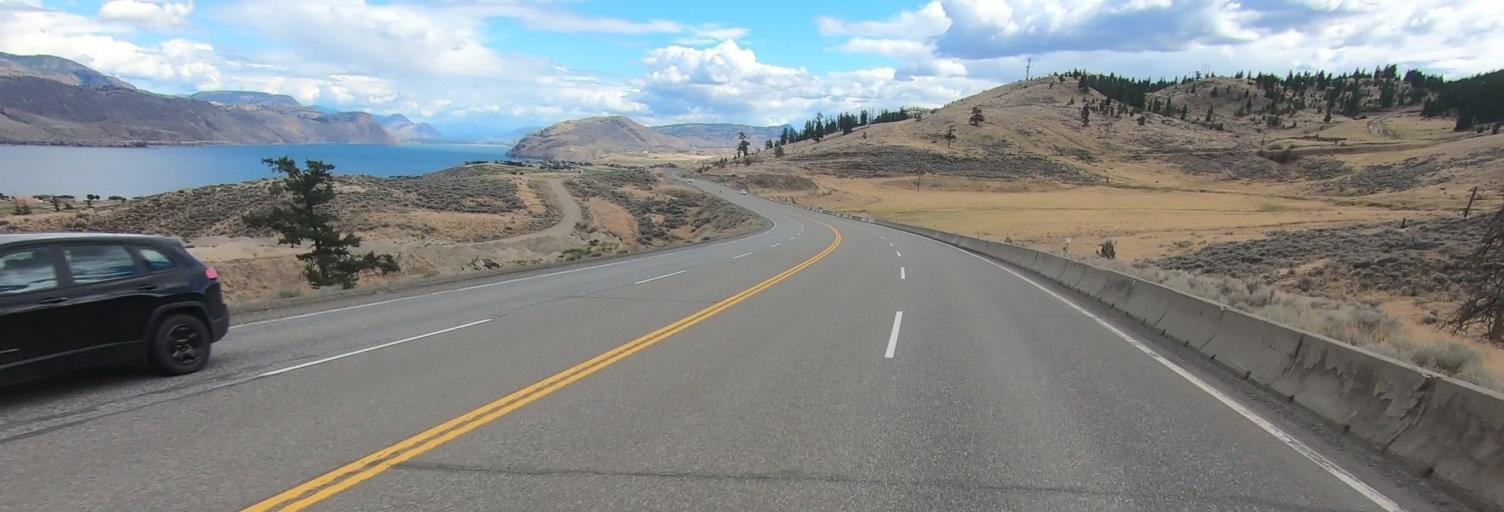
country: CA
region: British Columbia
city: Logan Lake
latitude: 50.7401
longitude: -120.7186
